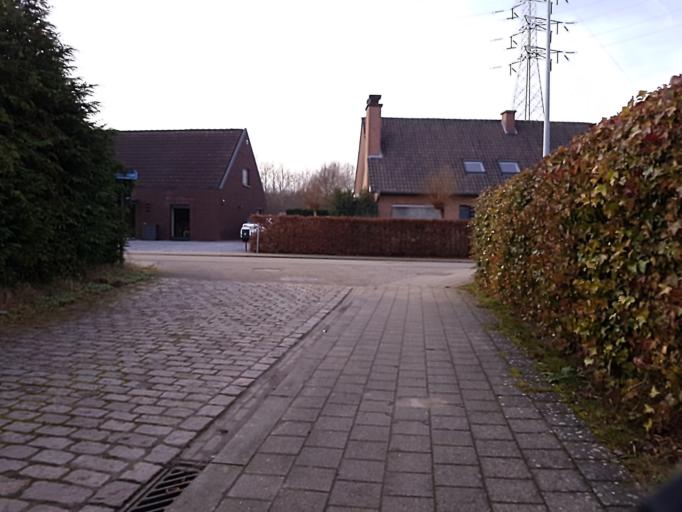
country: BE
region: Flanders
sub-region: Provincie Vlaams-Brabant
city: Rotselaar
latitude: 50.9321
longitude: 4.7082
